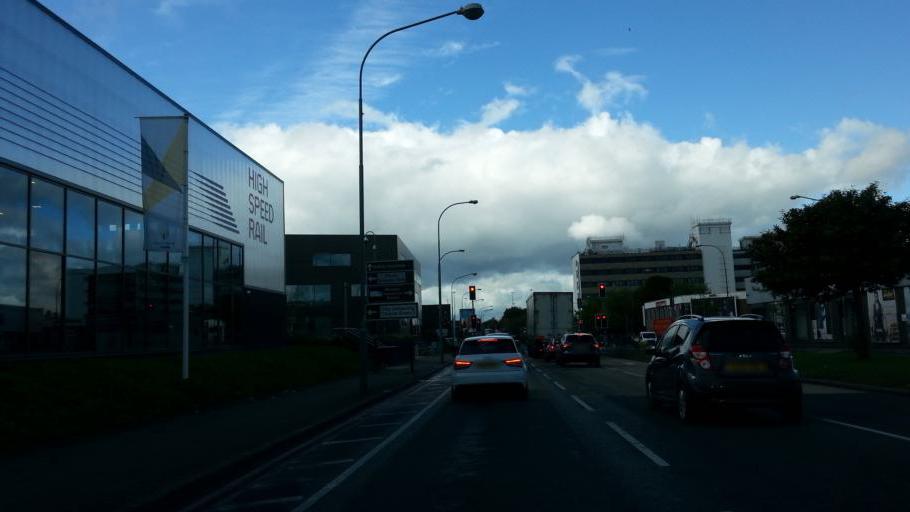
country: GB
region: England
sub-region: City and Borough of Birmingham
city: Birmingham
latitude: 52.4884
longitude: -1.8849
